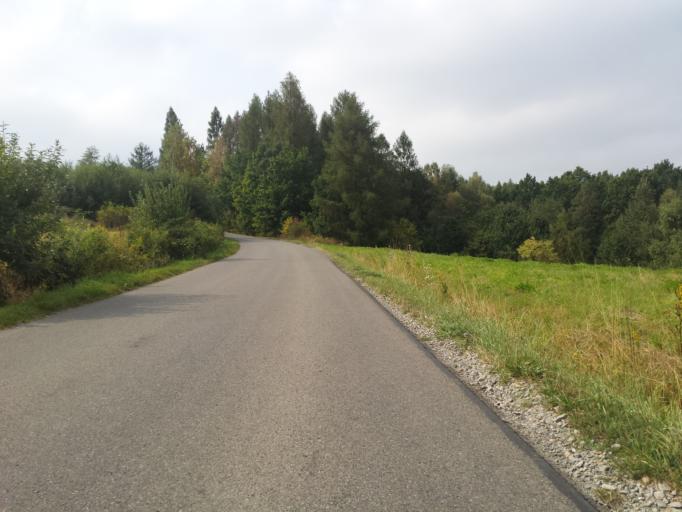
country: PL
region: Subcarpathian Voivodeship
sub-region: Powiat rzeszowski
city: Tyczyn
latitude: 49.9391
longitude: 22.0714
